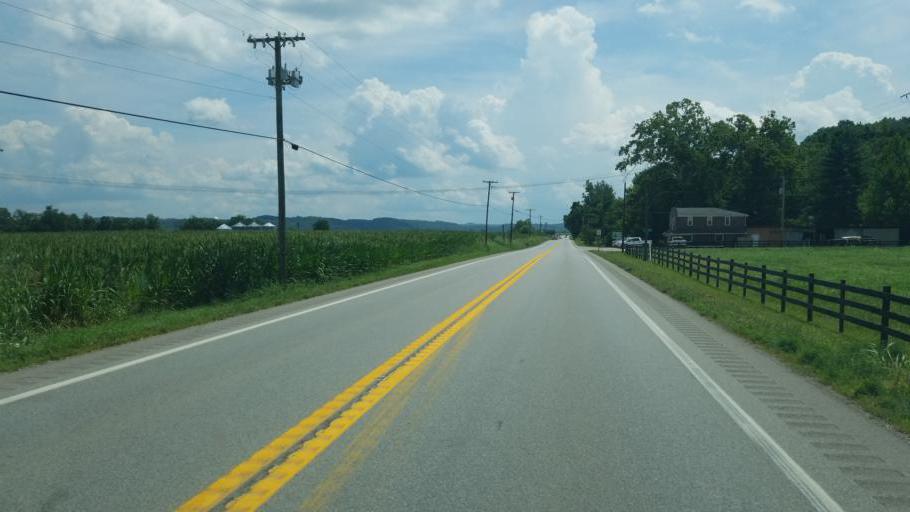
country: US
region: West Virginia
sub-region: Putnam County
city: Buffalo
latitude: 38.7458
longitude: -81.9815
